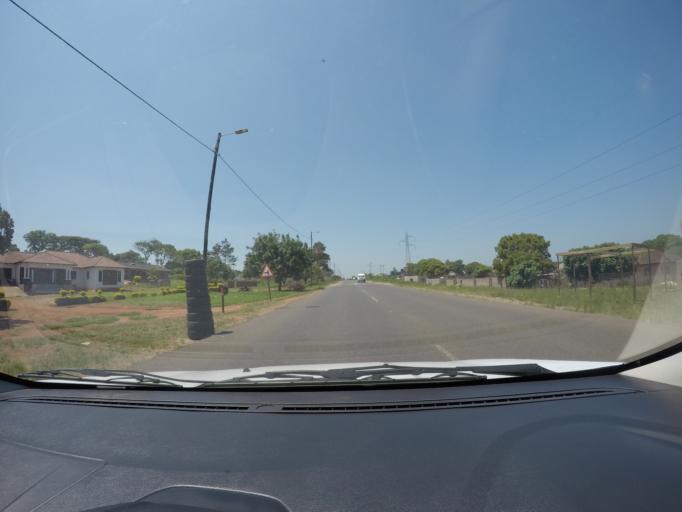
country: ZA
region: KwaZulu-Natal
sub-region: uThungulu District Municipality
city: eSikhawini
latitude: -28.8424
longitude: 31.9343
